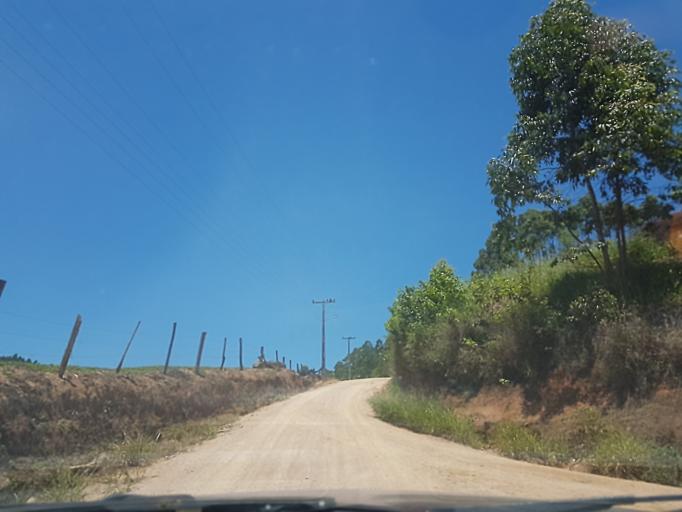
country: BR
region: Santa Catarina
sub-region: Braco Do Norte
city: Braco do Norte
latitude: -28.3891
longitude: -49.1289
